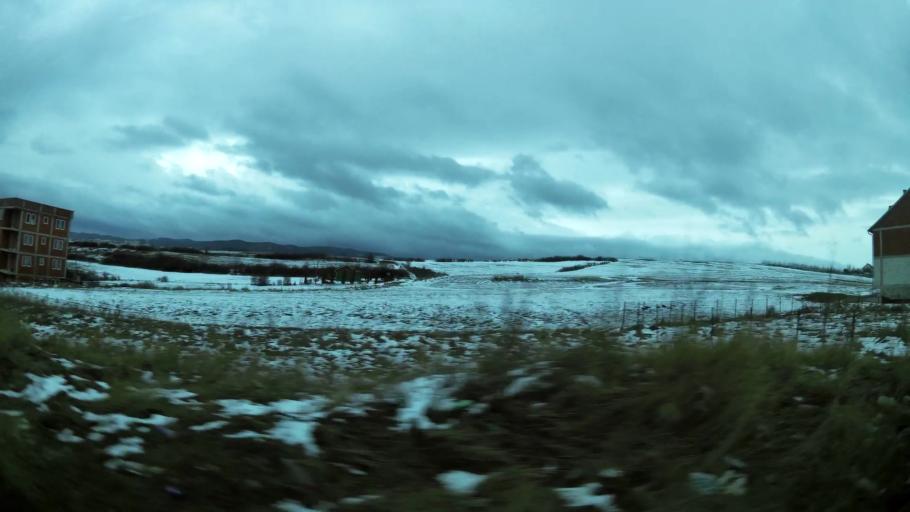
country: XK
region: Pristina
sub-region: Komuna e Prishtines
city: Pristina
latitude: 42.6363
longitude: 21.1656
